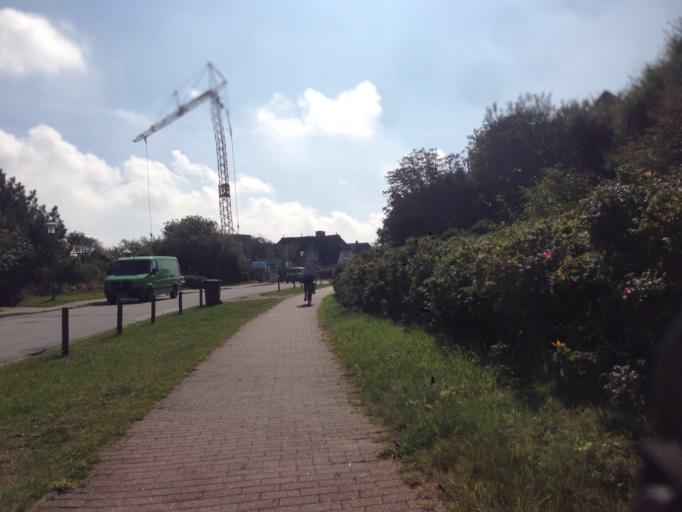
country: DE
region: Schleswig-Holstein
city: Westerland
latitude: 54.8494
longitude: 8.2939
